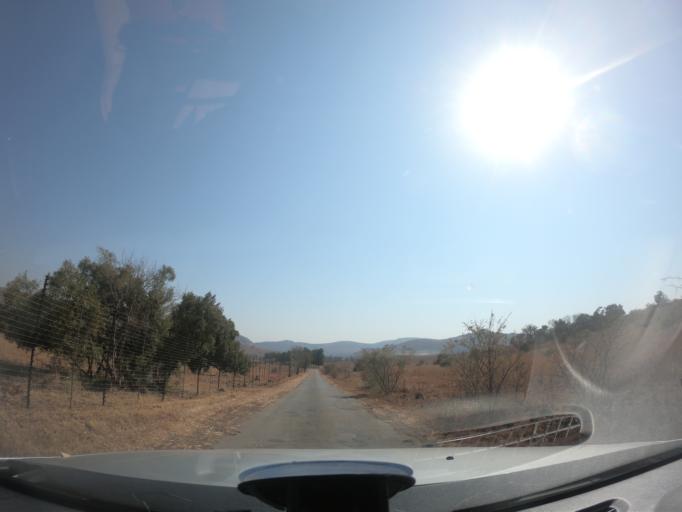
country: ZA
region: Gauteng
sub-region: City of Johannesburg Metropolitan Municipality
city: Diepsloot
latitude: -25.8384
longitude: 28.0315
